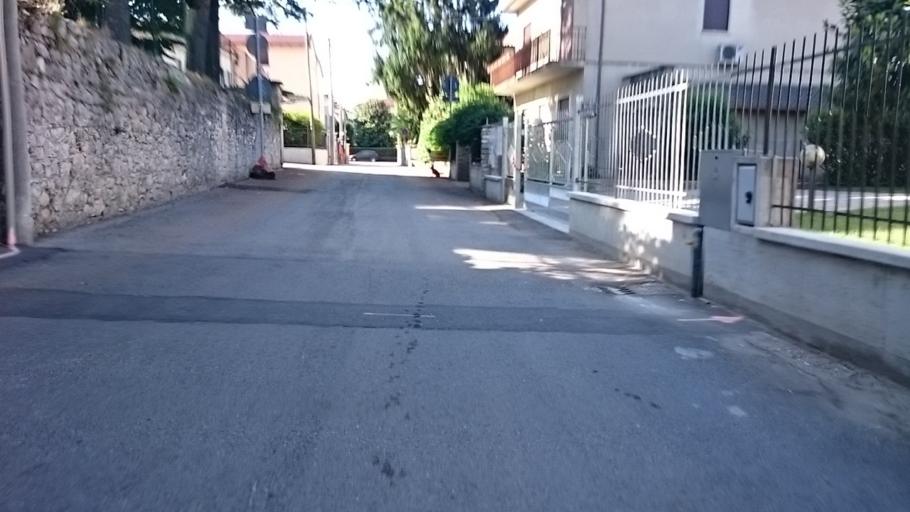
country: IT
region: Veneto
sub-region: Provincia di Vicenza
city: Vicenza
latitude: 45.5273
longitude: 11.5600
